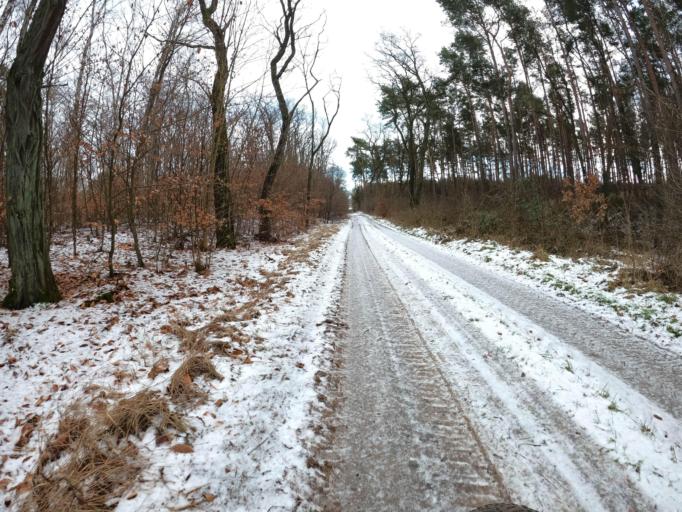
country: PL
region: Lubusz
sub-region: Powiat slubicki
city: Cybinka
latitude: 52.2034
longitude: 14.8546
